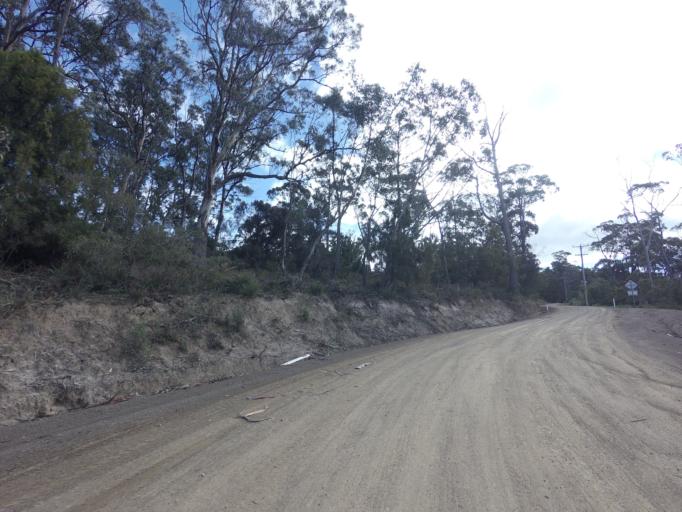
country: AU
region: Tasmania
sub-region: Clarence
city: Sandford
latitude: -43.0956
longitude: 147.7195
